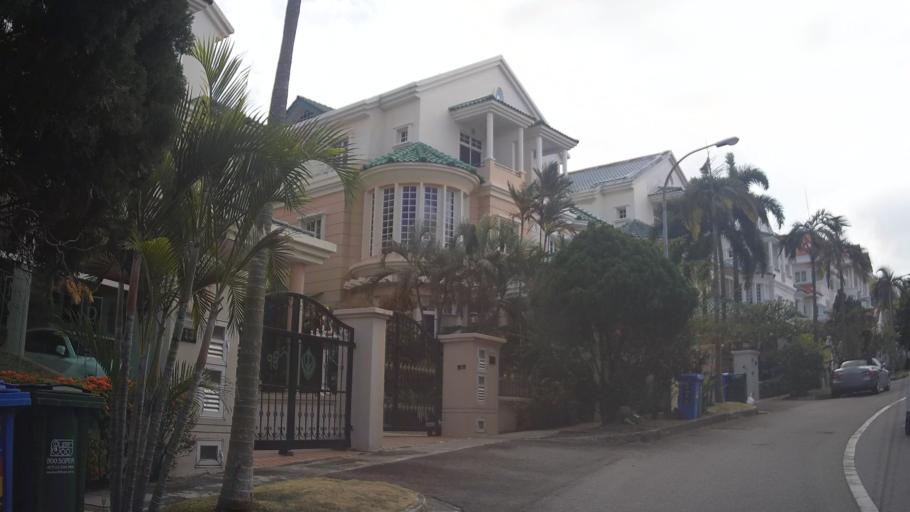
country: SG
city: Singapore
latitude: 1.3202
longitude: 103.9500
